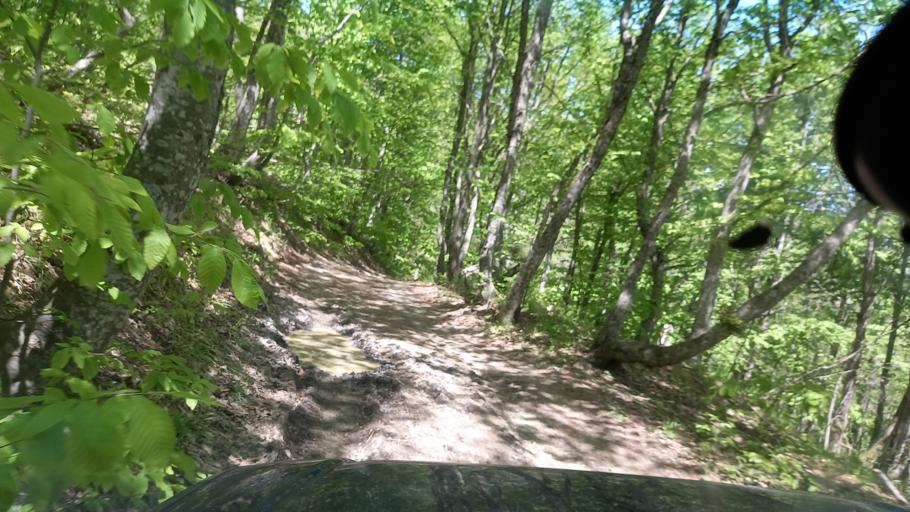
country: RU
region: Krasnodarskiy
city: Tuapse
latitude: 44.2462
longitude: 39.2924
